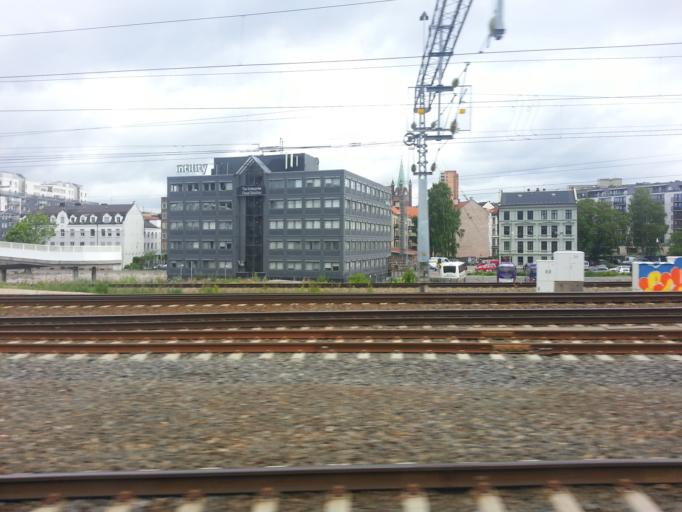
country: NO
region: Oslo
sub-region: Oslo
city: Oslo
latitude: 59.9083
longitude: 10.7654
